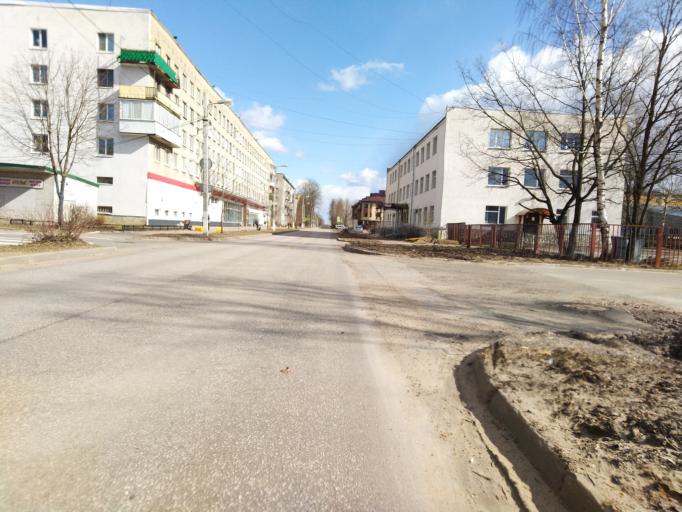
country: RU
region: Leningrad
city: Novoye Devyatkino
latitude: 60.1081
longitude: 30.4863
